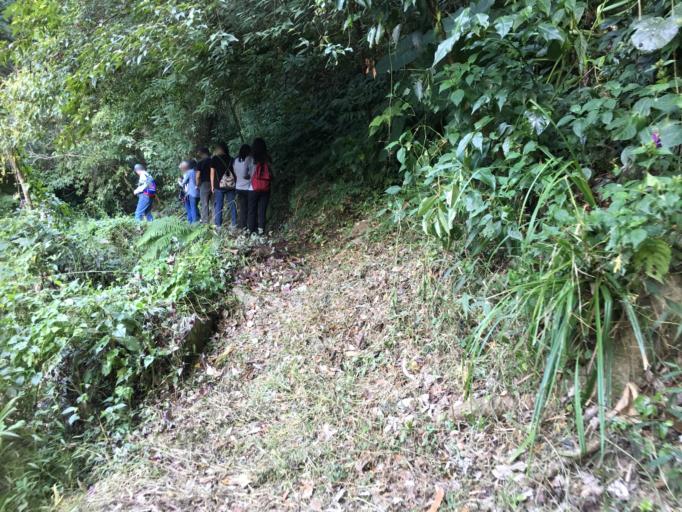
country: TW
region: Taiwan
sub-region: Nantou
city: Puli
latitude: 23.9514
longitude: 121.0709
